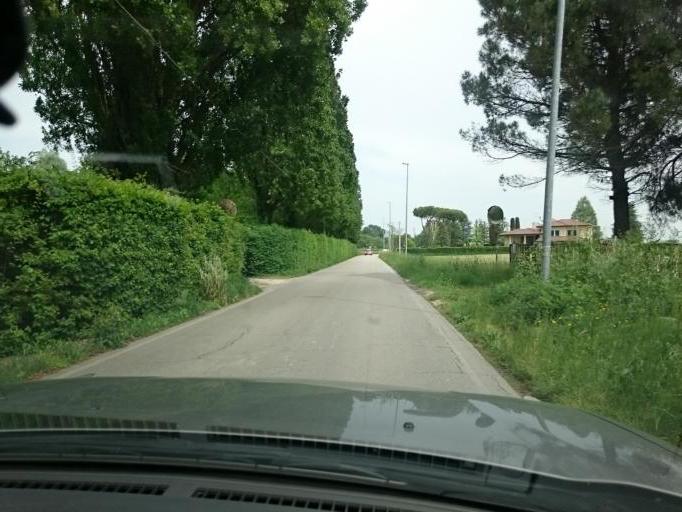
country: IT
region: Veneto
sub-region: Provincia di Venezia
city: Fiesso
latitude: 45.4139
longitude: 12.0328
